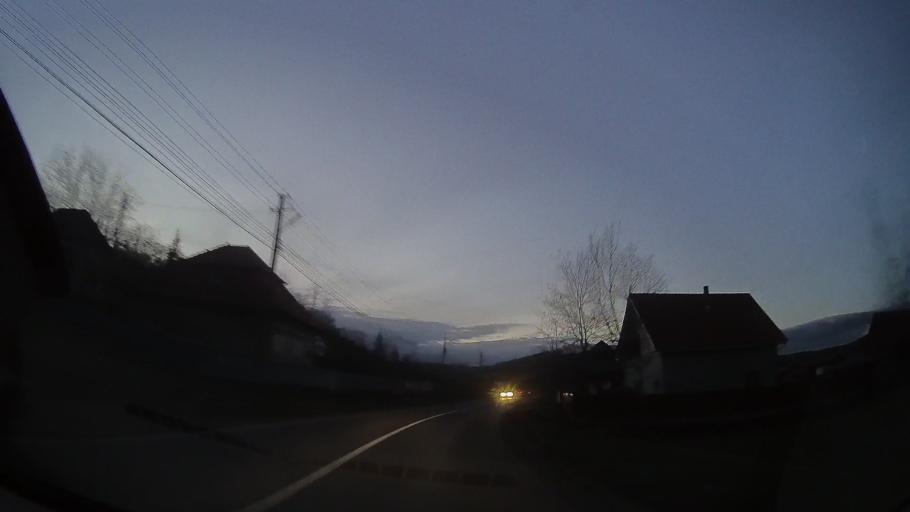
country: RO
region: Mures
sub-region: Comuna Sarmasu
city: Sarmasu
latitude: 46.7635
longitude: 24.1847
